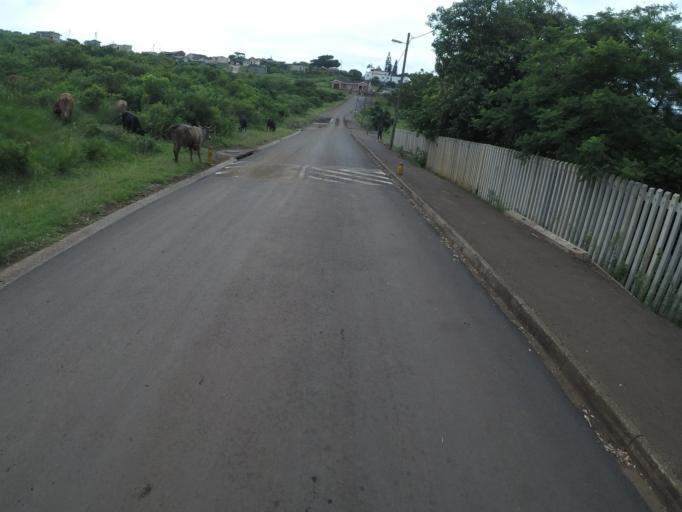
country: ZA
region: KwaZulu-Natal
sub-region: uThungulu District Municipality
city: Empangeni
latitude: -28.7705
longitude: 31.8598
